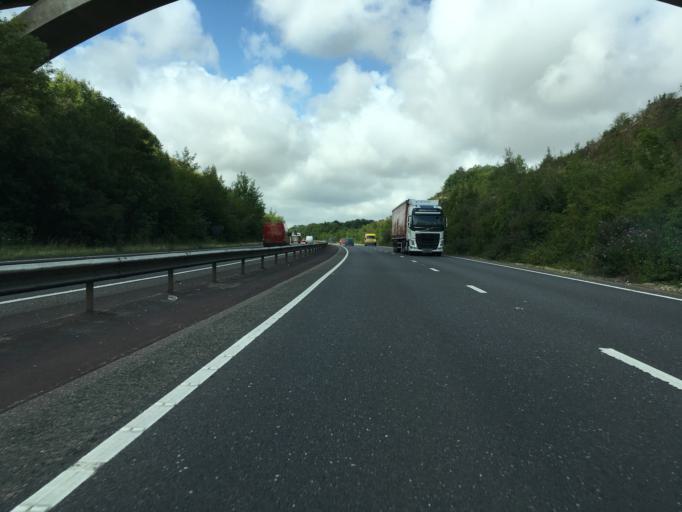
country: GB
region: England
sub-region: East Sussex
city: Lewes
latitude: 50.8672
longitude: -0.0041
